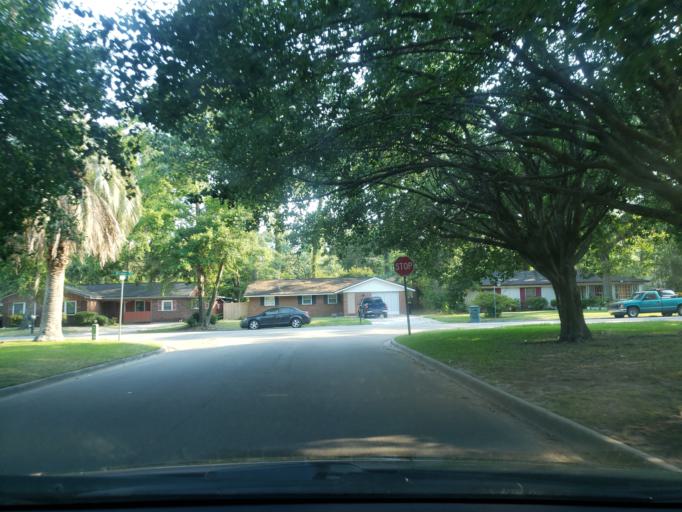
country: US
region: Georgia
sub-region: Chatham County
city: Montgomery
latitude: 31.9862
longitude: -81.1413
